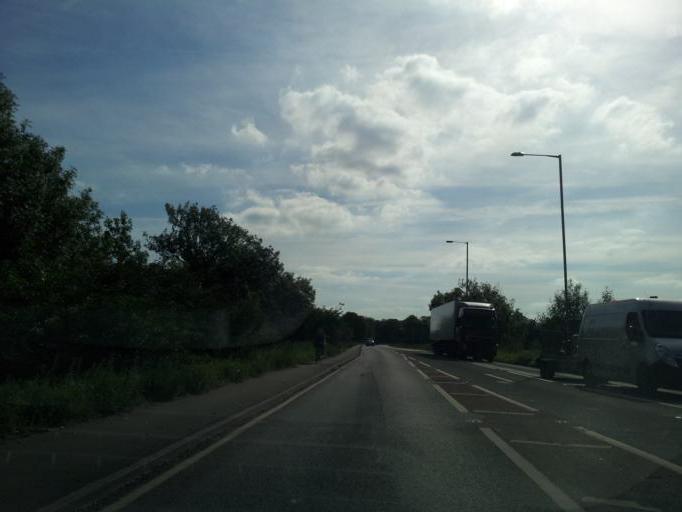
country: GB
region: England
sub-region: Cambridgeshire
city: Waterbeach
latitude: 52.2710
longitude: 0.1784
